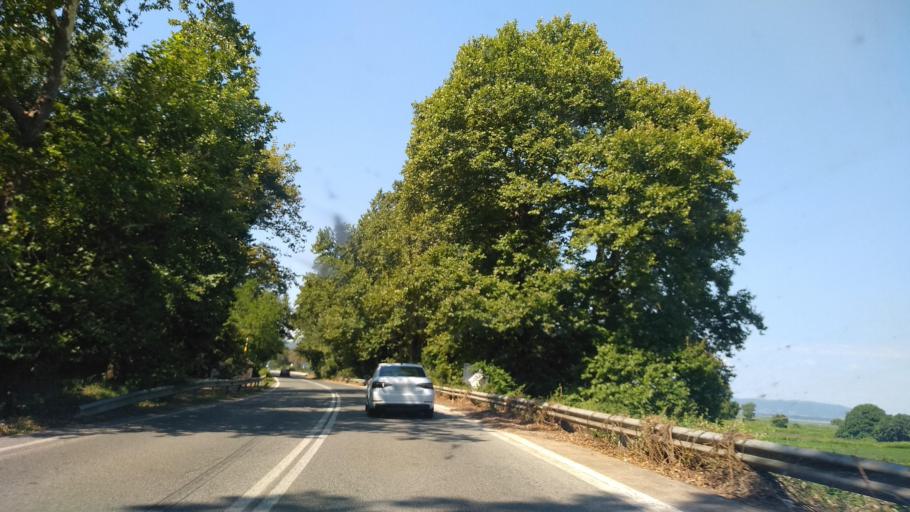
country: GR
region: Central Macedonia
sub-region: Nomos Thessalonikis
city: Stavros
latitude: 40.6536
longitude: 23.6106
